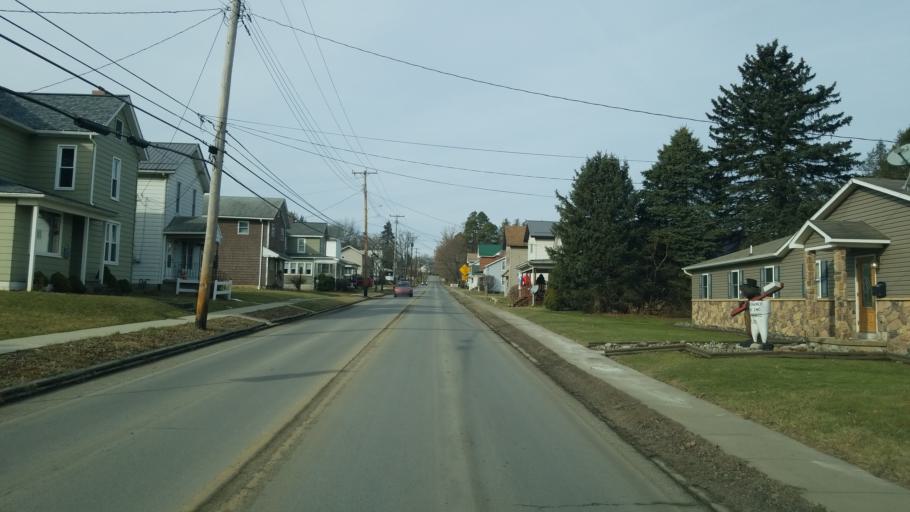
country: US
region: Pennsylvania
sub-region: Jefferson County
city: Punxsutawney
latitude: 40.9454
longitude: -78.9930
